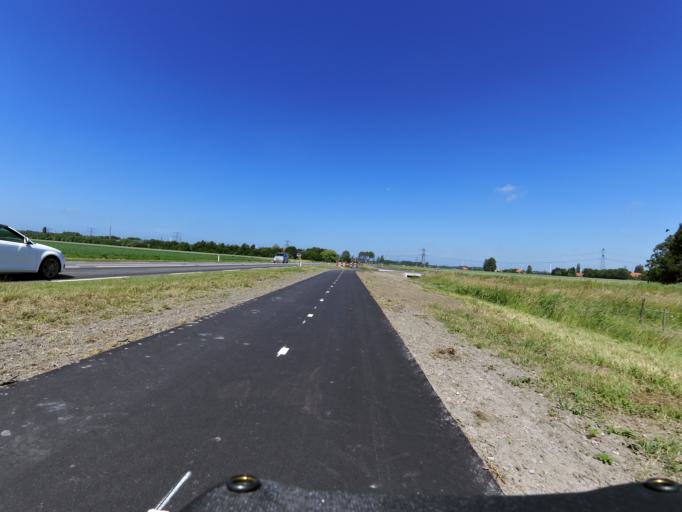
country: NL
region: South Holland
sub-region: Gemeente Brielle
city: Brielle
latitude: 51.9067
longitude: 4.1181
